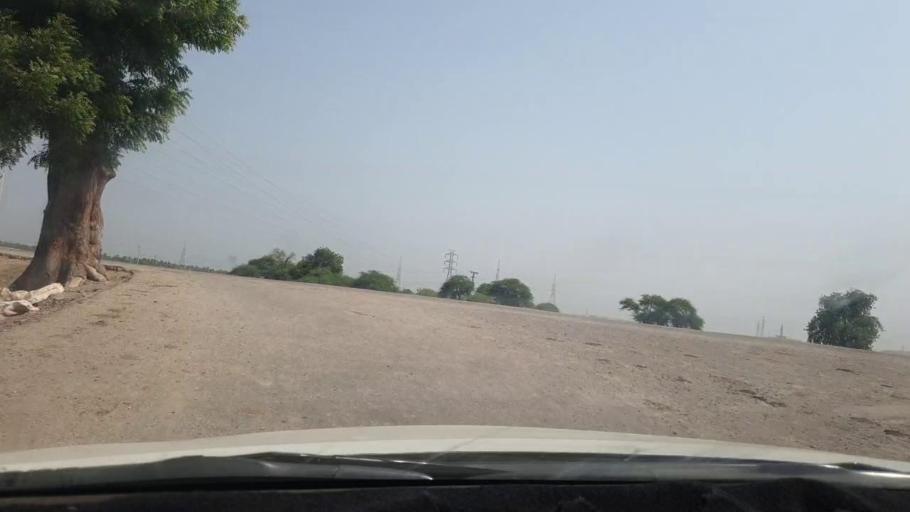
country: PK
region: Sindh
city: Rohri
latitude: 27.6384
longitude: 68.8841
